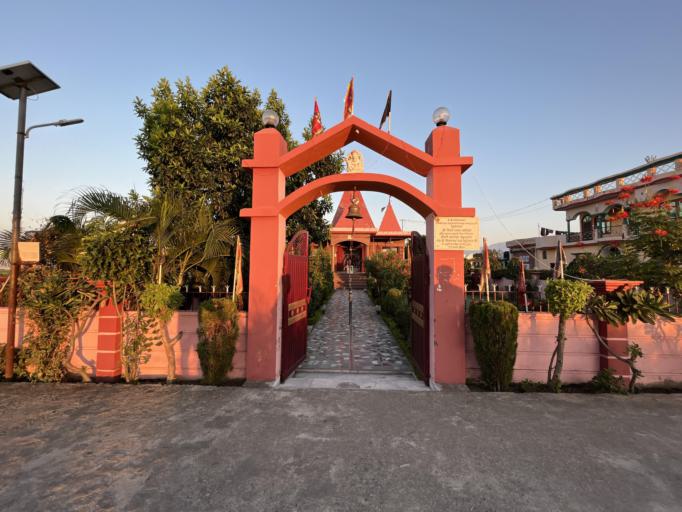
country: IN
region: Uttarakhand
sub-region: Naini Tal
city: Haldwani
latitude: 29.1974
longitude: 79.4923
